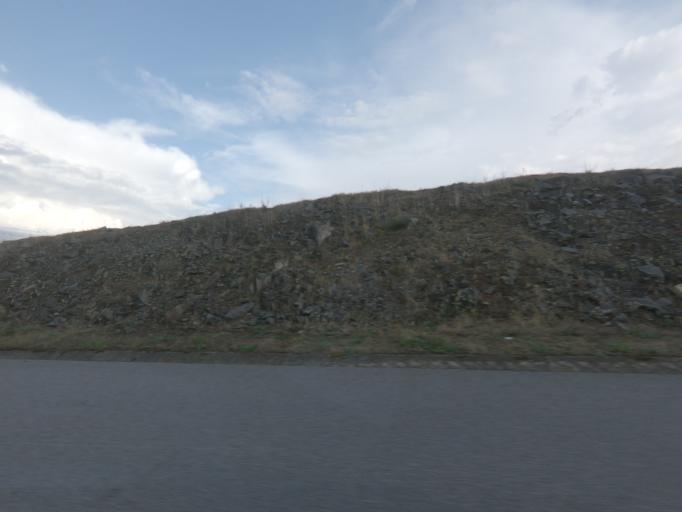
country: PT
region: Viseu
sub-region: Castro Daire
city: Castro Daire
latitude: 40.9493
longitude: -7.8955
